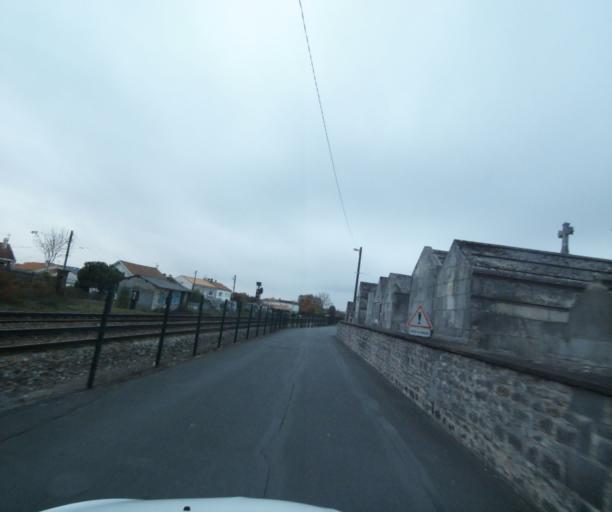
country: FR
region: Poitou-Charentes
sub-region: Departement de la Charente-Maritime
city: Saintes
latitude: 45.7417
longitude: -0.6181
